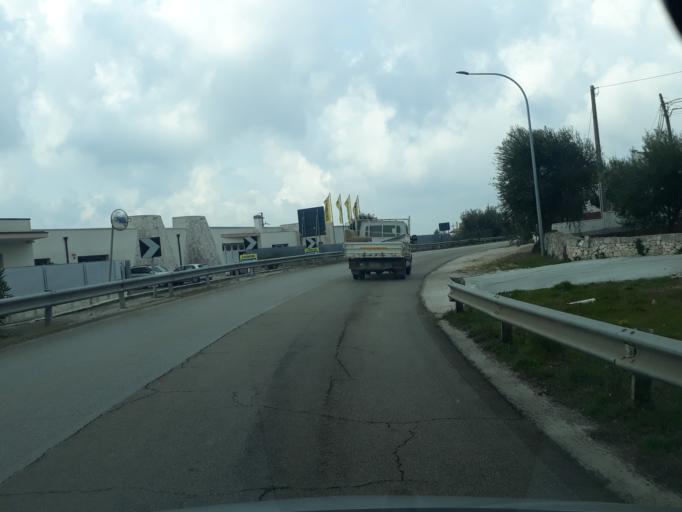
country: IT
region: Apulia
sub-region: Provincia di Brindisi
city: Cisternino
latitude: 40.7446
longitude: 17.4032
